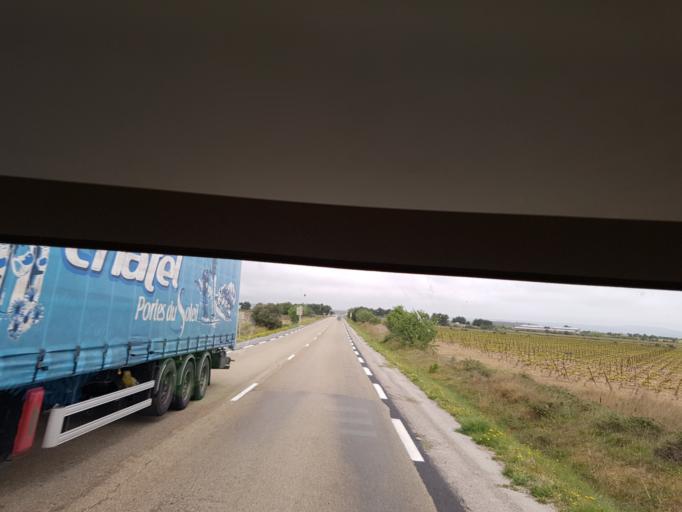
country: FR
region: Languedoc-Roussillon
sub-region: Departement de l'Aude
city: Leucate
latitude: 42.9267
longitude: 2.9942
